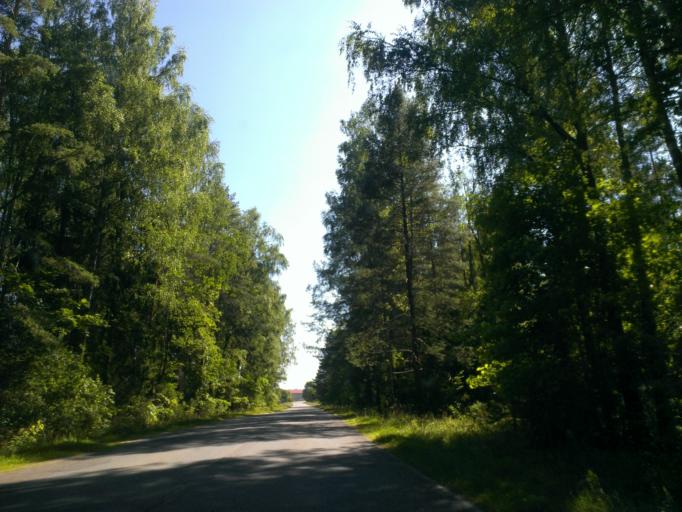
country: LV
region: Sigulda
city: Sigulda
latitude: 57.1073
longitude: 24.8255
